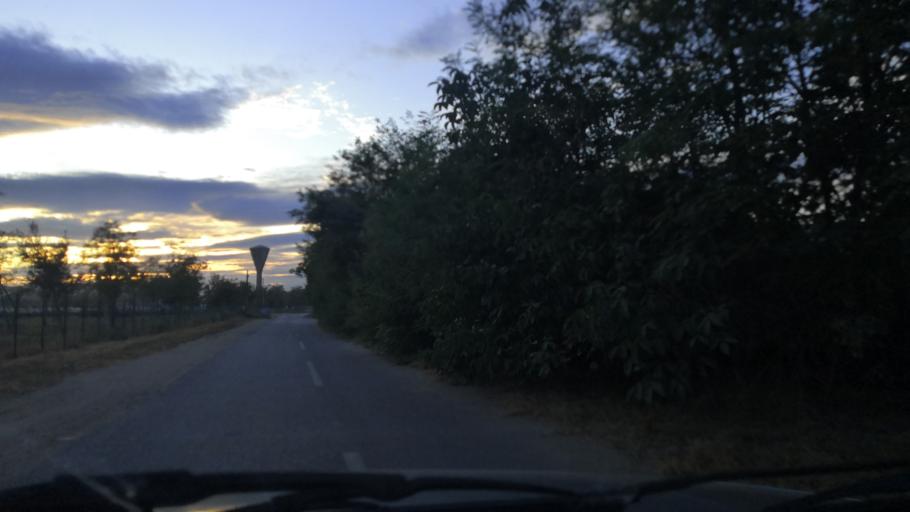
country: RO
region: Mehedinti
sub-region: Comuna Gruia
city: Izvoarele
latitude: 44.2887
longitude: 22.6137
